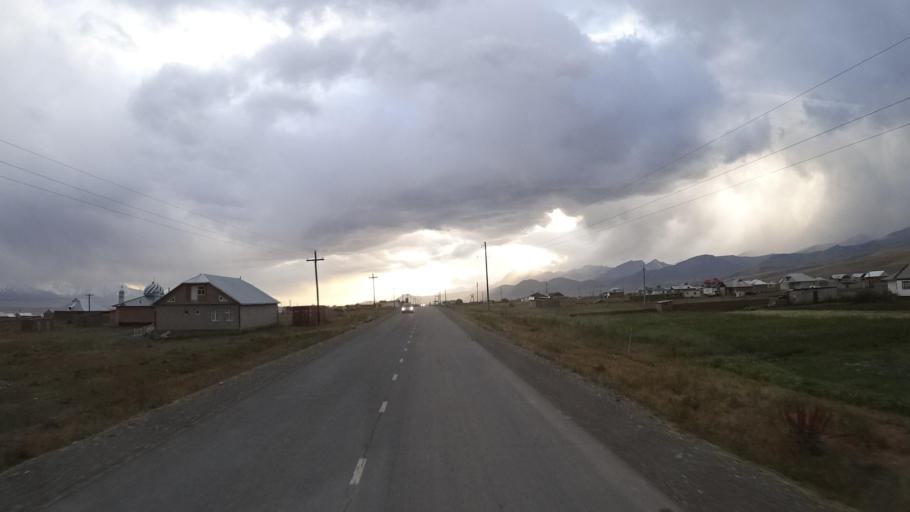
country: KG
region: Osh
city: Osh
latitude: 39.6782
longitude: 72.8923
